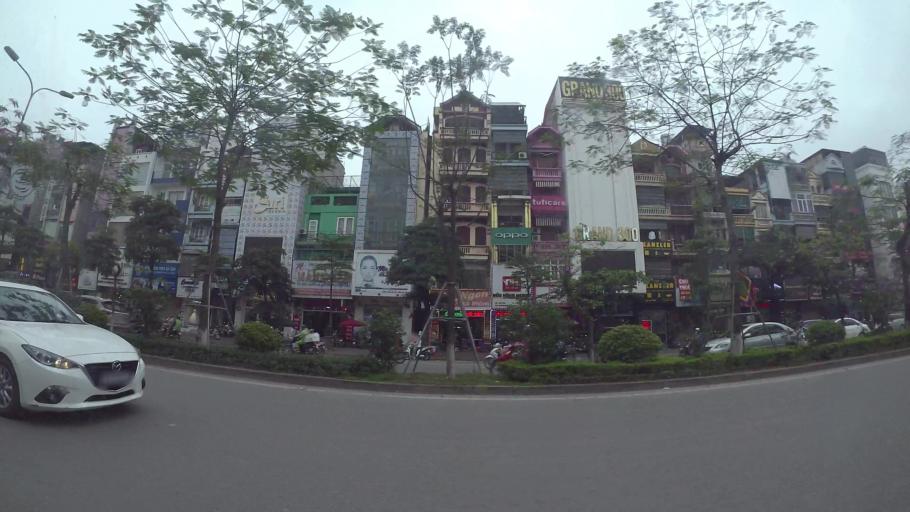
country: VN
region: Ha Noi
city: Dong Da
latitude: 21.0132
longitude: 105.8352
